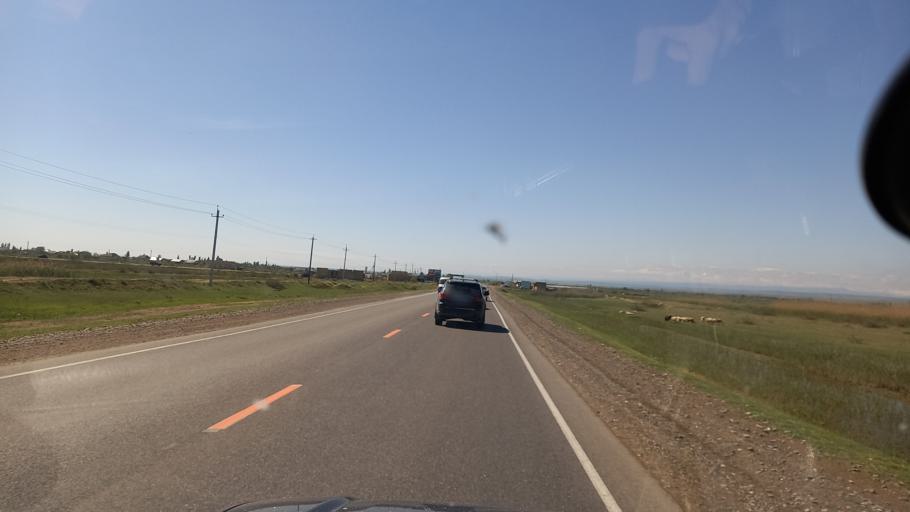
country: RU
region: Dagestan
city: Khazar
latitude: 41.9432
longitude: 48.3262
